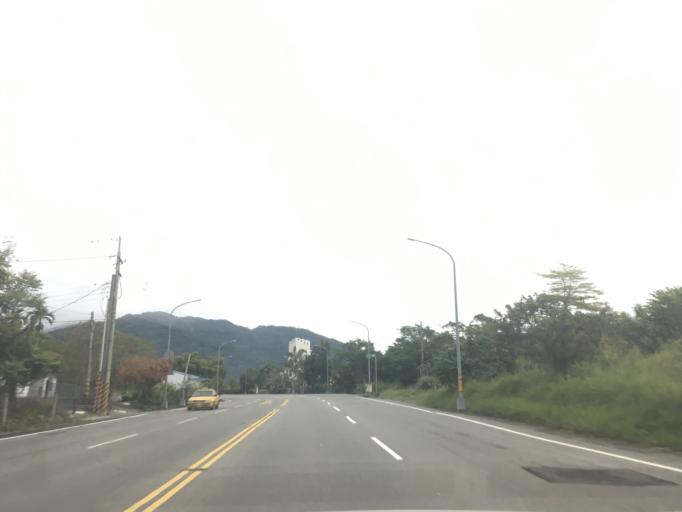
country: TW
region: Taiwan
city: Taitung City
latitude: 22.7454
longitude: 121.0570
